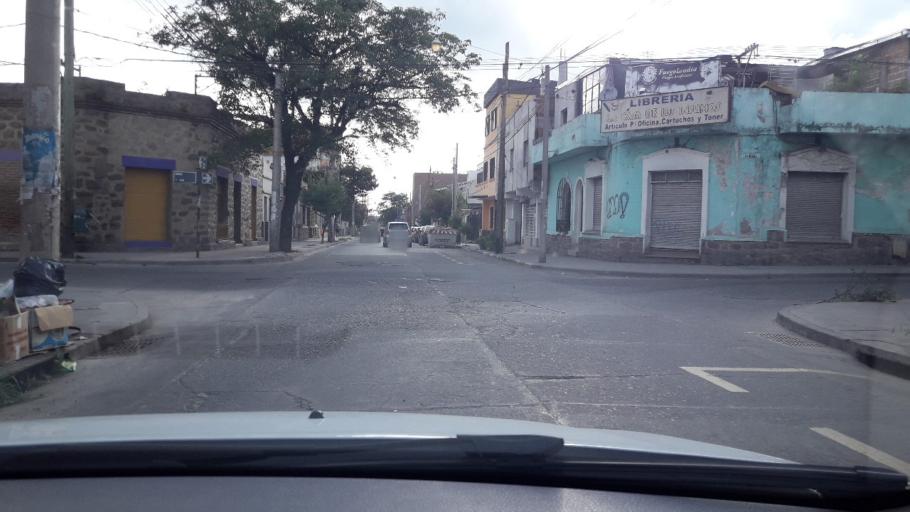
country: AR
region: Jujuy
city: San Salvador de Jujuy
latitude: -24.1908
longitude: -65.3065
